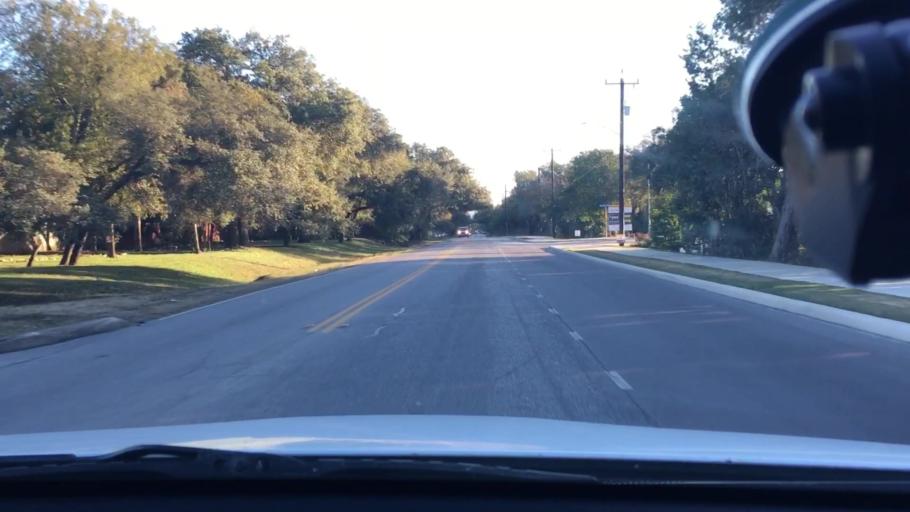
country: US
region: Texas
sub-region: Bexar County
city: Live Oak
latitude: 29.5916
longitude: -98.3687
